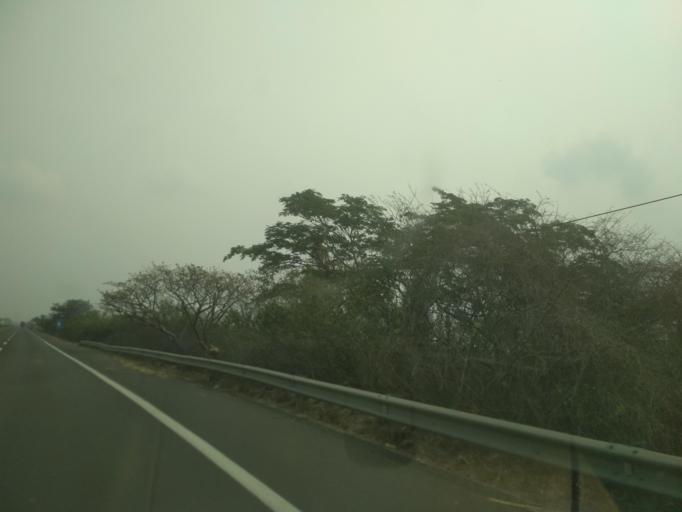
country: MX
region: Veracruz
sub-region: Veracruz
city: Delfino Victoria (Santa Fe)
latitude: 19.2235
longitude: -96.2550
